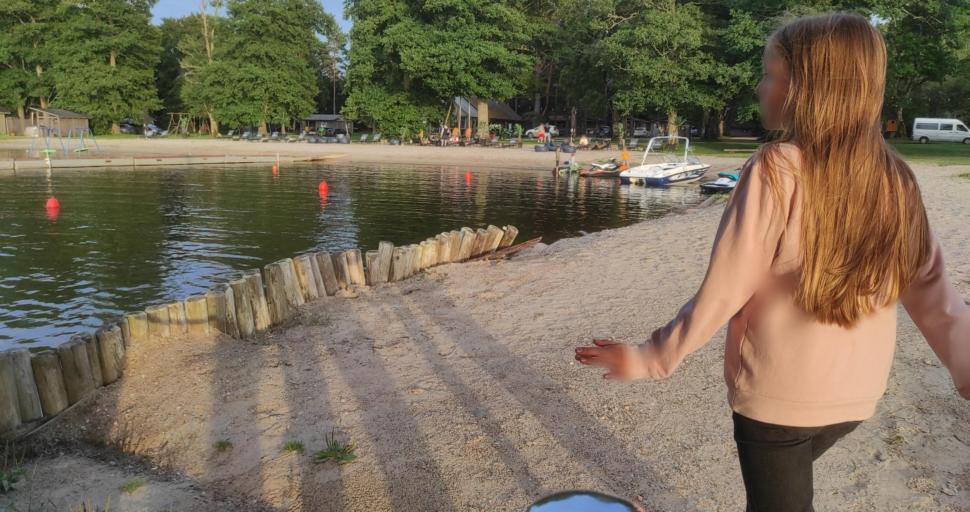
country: LV
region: Kuldigas Rajons
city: Kuldiga
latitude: 57.1235
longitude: 22.1882
